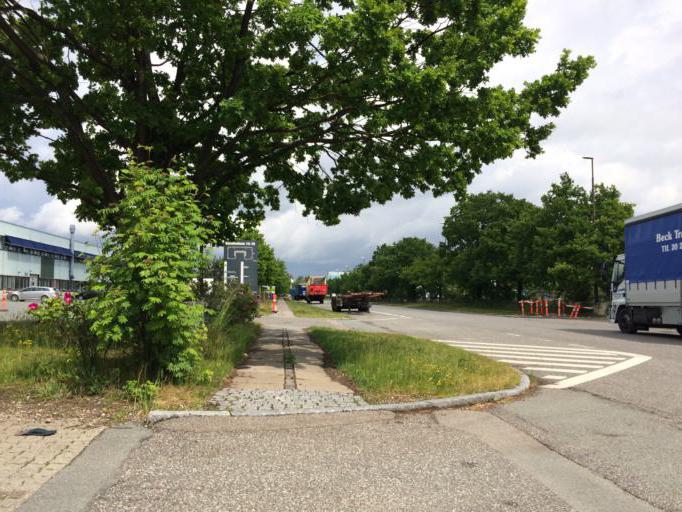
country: DK
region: Capital Region
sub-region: Hvidovre Kommune
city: Hvidovre
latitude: 55.6103
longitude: 12.4531
